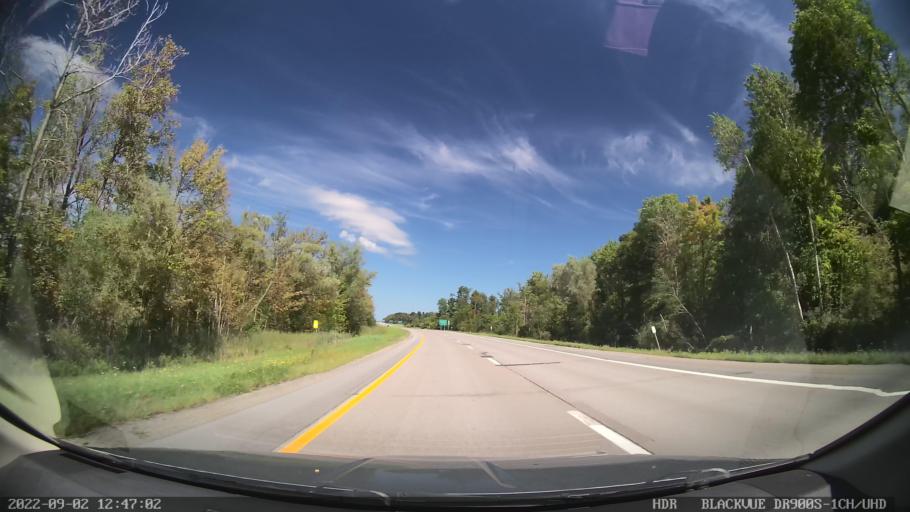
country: US
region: New York
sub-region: Livingston County
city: Livonia
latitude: 42.8082
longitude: -77.7382
